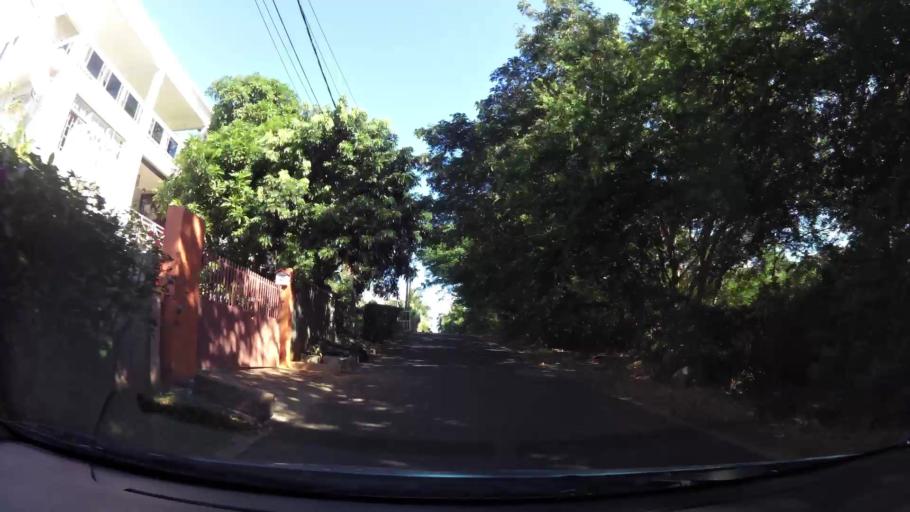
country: MU
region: Black River
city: Albion
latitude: -20.2179
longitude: 57.4036
